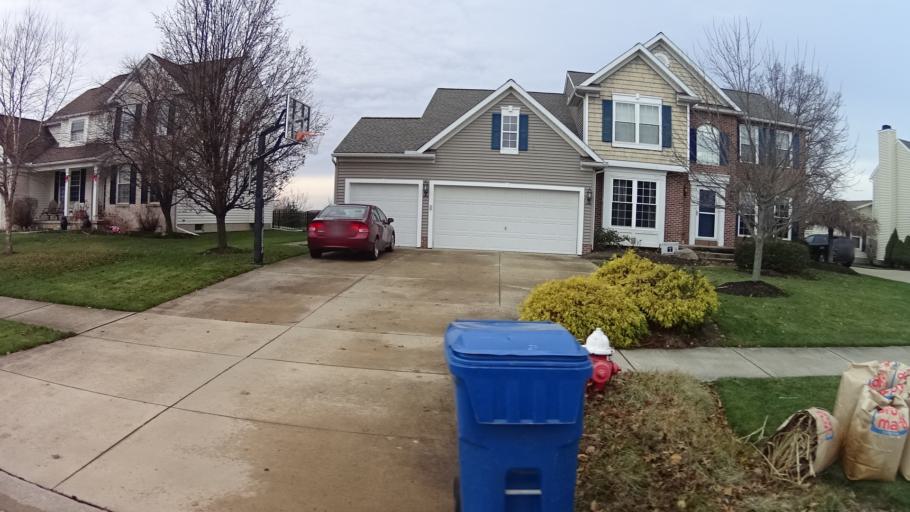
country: US
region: Ohio
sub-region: Lorain County
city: North Ridgeville
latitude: 41.3583
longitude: -82.0403
